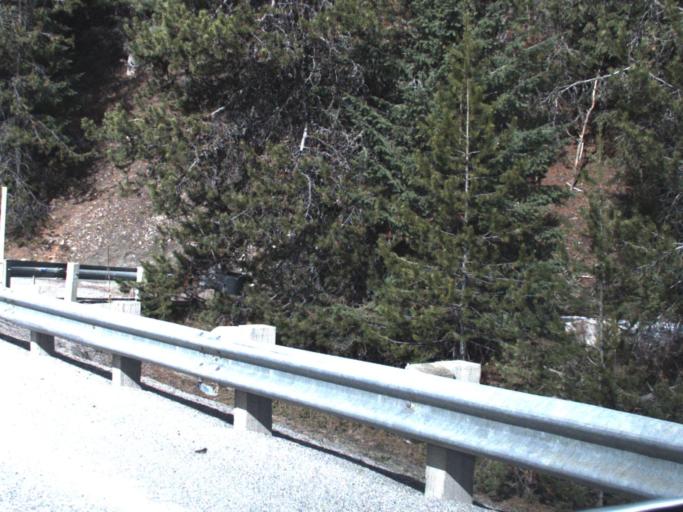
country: US
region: Washington
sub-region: Stevens County
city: Chewelah
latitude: 48.5440
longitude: -117.5860
